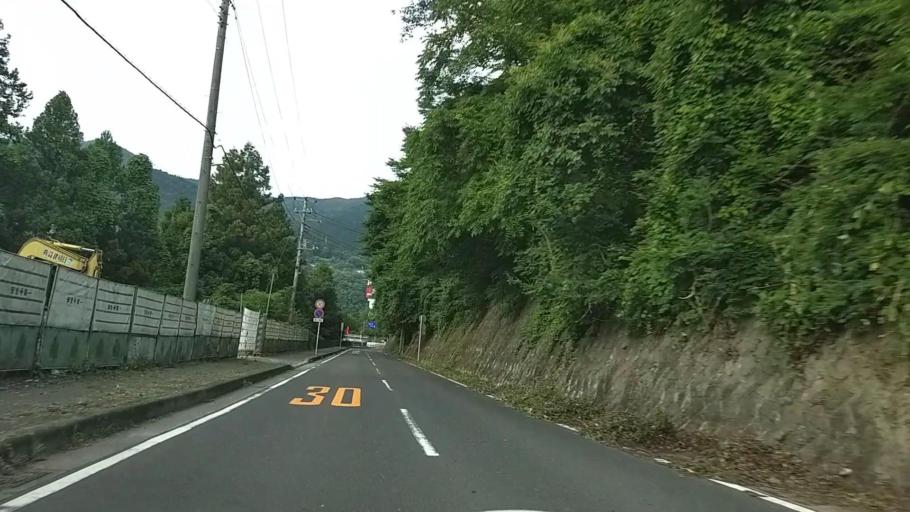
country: JP
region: Yamanashi
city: Uenohara
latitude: 35.6108
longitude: 139.1723
